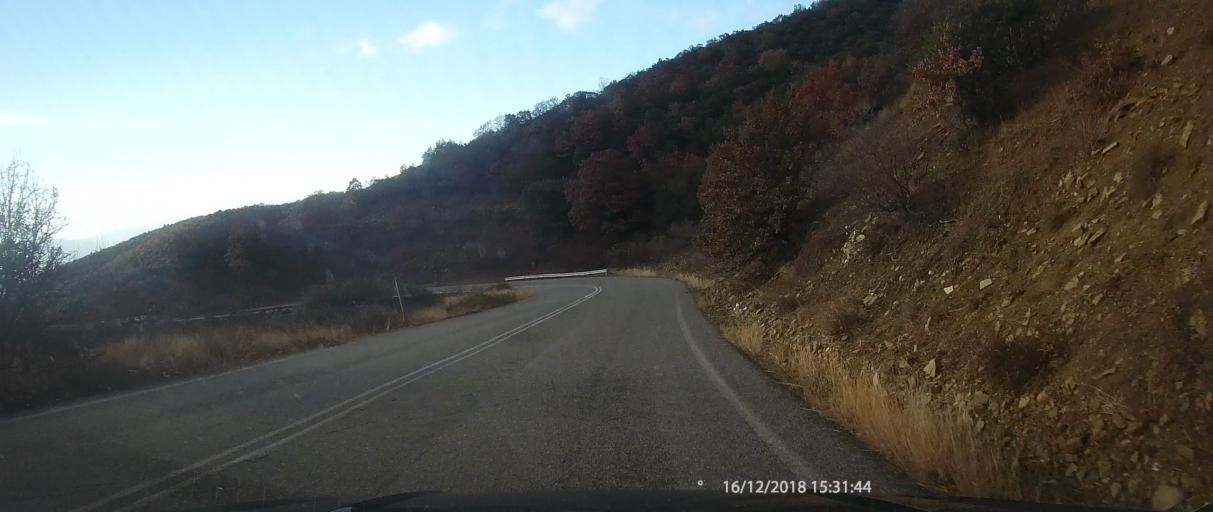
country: GR
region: Epirus
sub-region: Nomos Ioanninon
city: Konitsa
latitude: 40.0708
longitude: 20.7448
